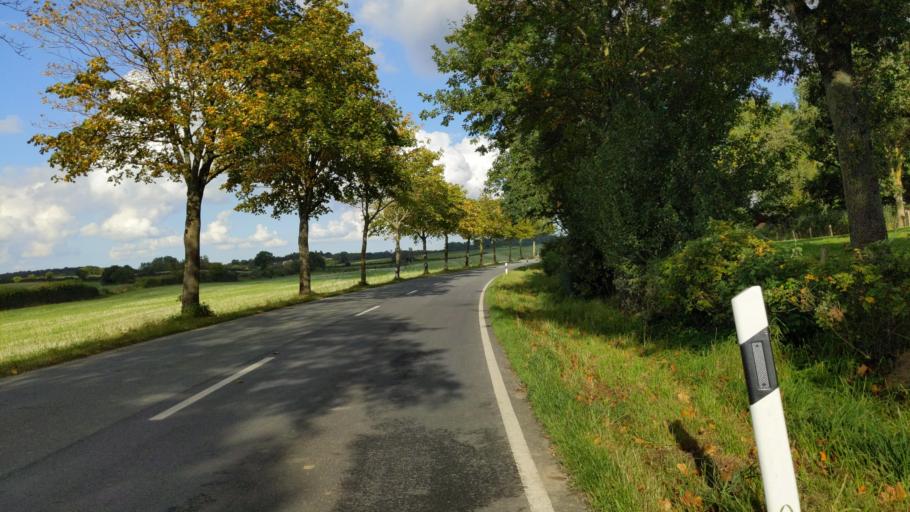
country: DE
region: Schleswig-Holstein
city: Ahrensbok
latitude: 54.0164
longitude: 10.5867
